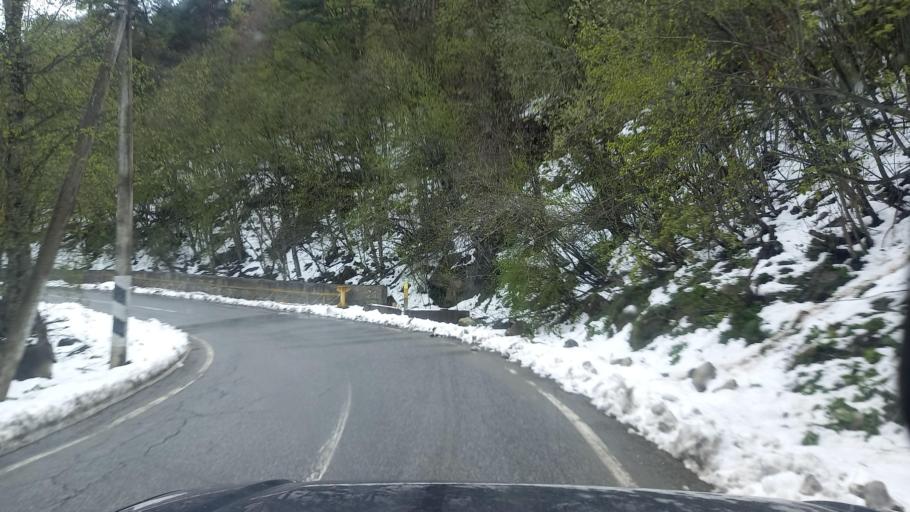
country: RU
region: North Ossetia
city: Mizur
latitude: 42.7914
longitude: 43.9104
